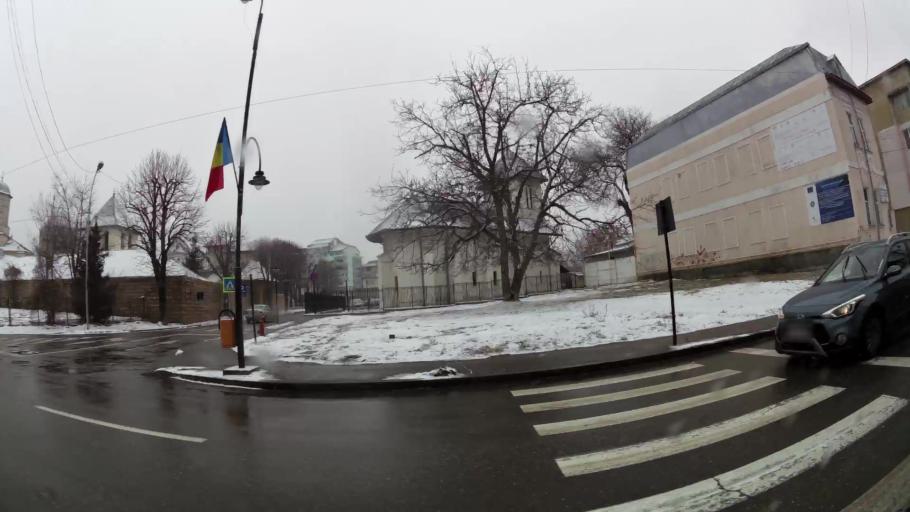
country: RO
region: Dambovita
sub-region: Municipiul Targoviste
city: Targoviste
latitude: 44.9297
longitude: 25.4615
